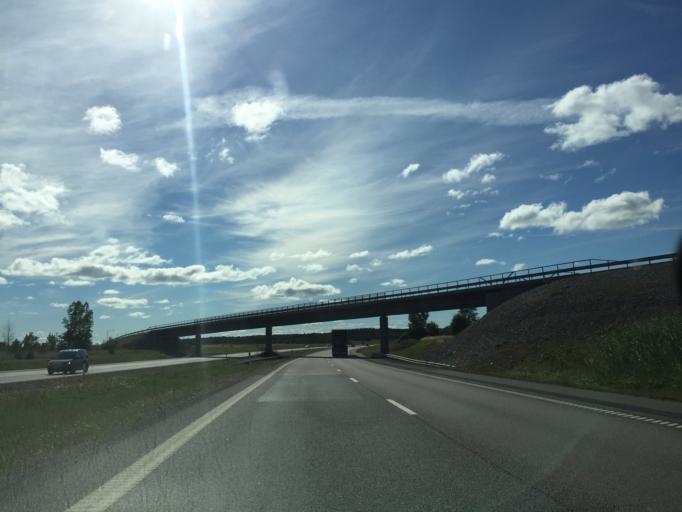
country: SE
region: Vaestmanland
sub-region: Arboga Kommun
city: Arboga
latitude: 59.4342
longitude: 15.8959
